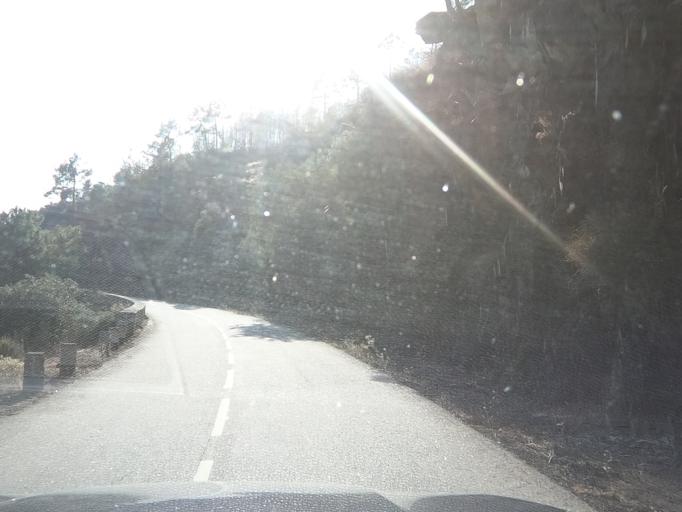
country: PT
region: Vila Real
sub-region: Sabrosa
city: Vilela
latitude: 41.2146
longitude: -7.6150
